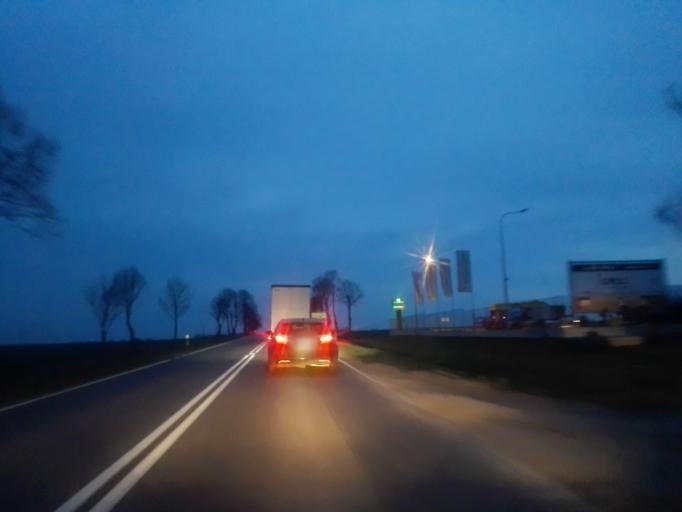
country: PL
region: Podlasie
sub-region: Lomza
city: Lomza
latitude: 53.1230
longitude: 22.0338
